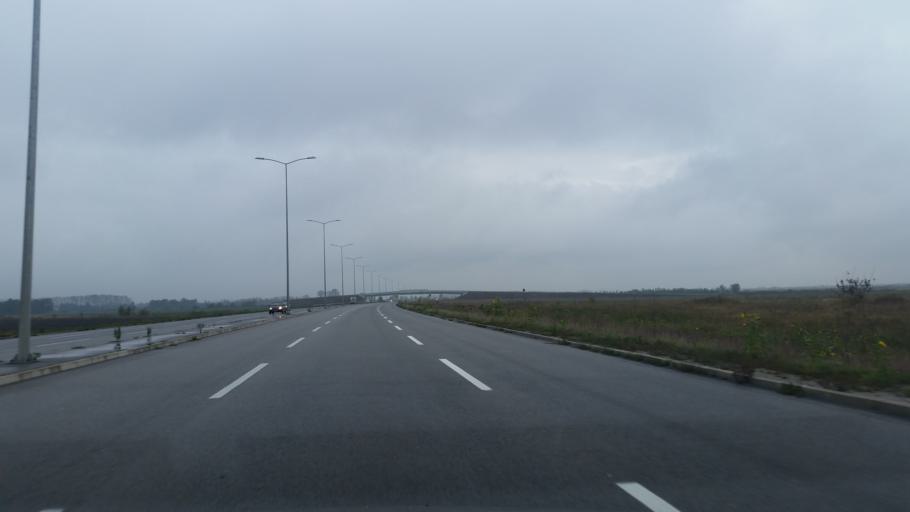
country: RS
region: Central Serbia
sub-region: Belgrade
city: Zemun
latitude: 44.8921
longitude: 20.4094
